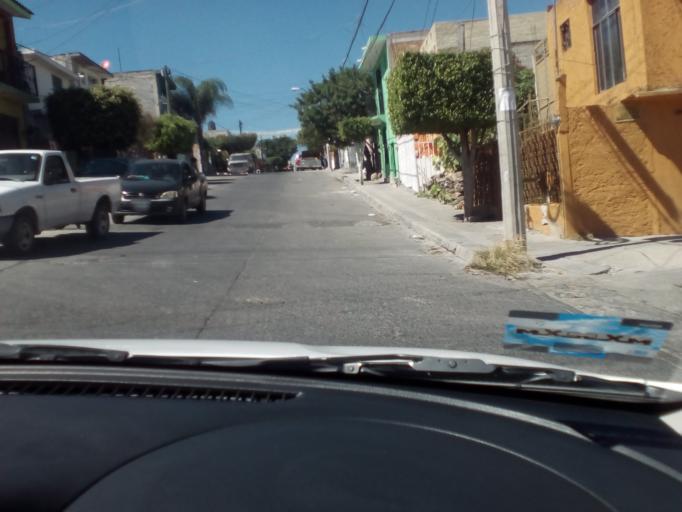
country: MX
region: Guanajuato
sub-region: Leon
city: Ejido la Joya
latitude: 21.1233
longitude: -101.7104
